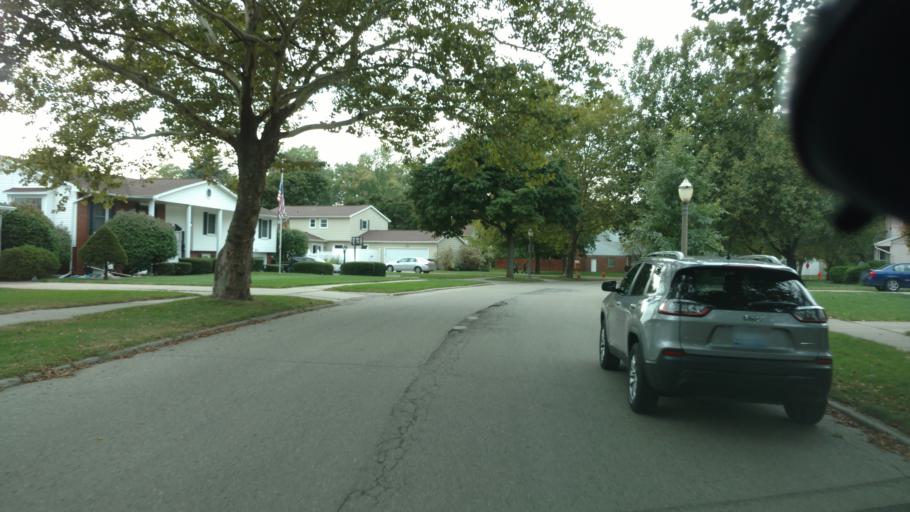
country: US
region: Michigan
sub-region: Ingham County
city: East Lansing
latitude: 42.7558
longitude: -84.5203
